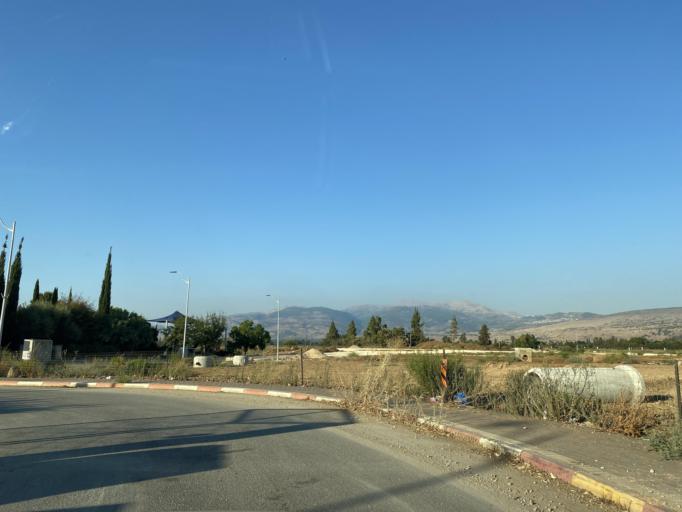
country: IL
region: Northern District
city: Qiryat Shemona
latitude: 33.1750
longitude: 35.6069
